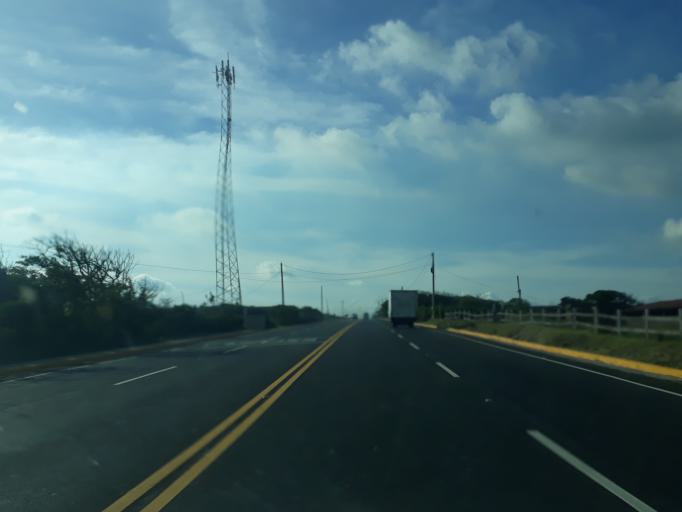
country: NI
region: Managua
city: El Crucero
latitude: 11.9252
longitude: -86.2832
